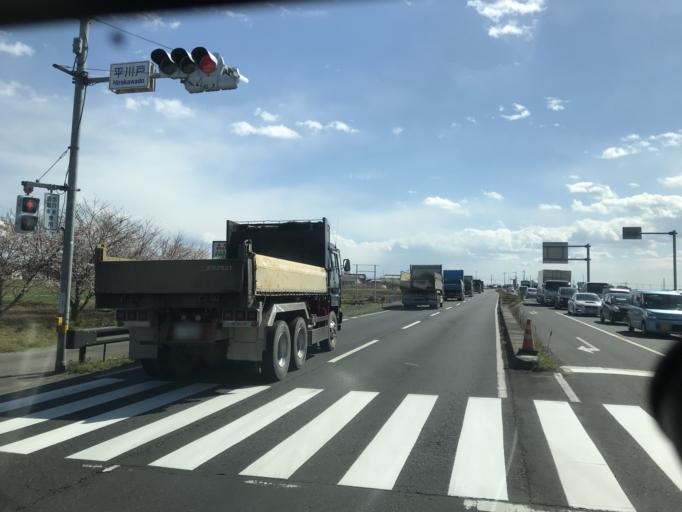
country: JP
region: Ibaraki
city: Ishige
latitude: 36.2052
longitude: 139.9845
